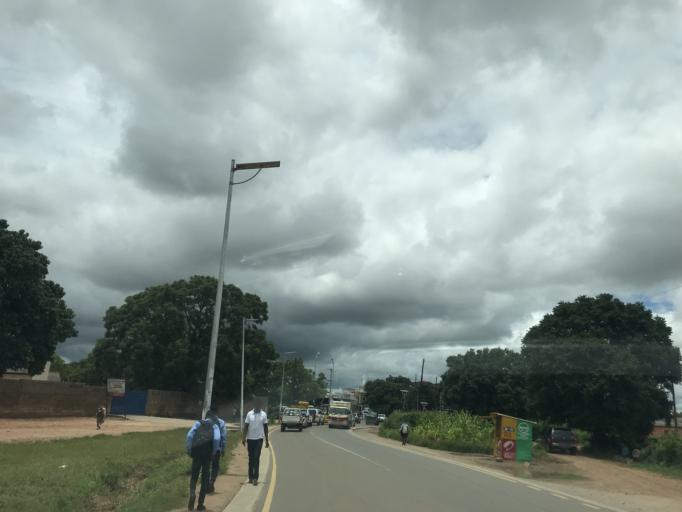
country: ZM
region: Lusaka
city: Lusaka
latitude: -15.4289
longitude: 28.3031
